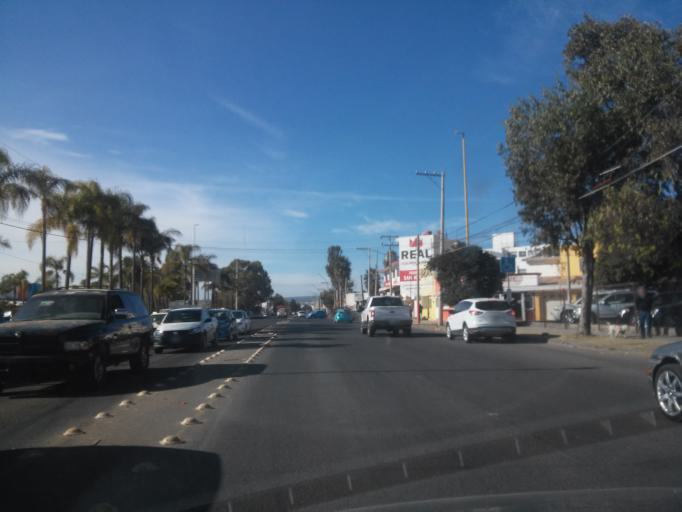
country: MX
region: Durango
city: Victoria de Durango
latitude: 24.0423
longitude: -104.6586
